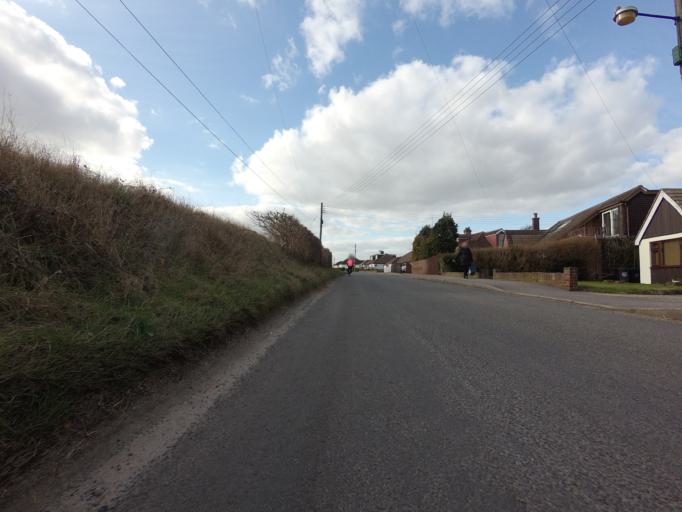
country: GB
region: England
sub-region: Kent
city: Dartford
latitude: 51.4212
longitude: 0.2196
